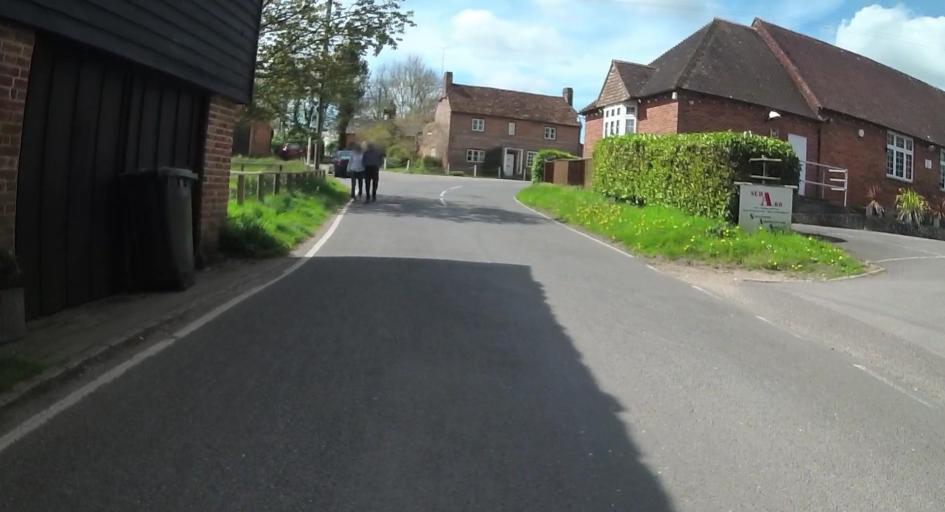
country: GB
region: England
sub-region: Hampshire
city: Romsey
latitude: 51.0397
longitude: -1.5378
